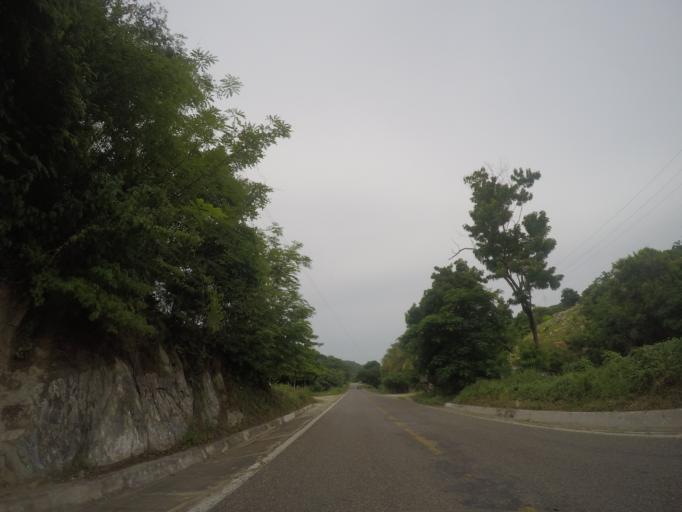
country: MX
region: Oaxaca
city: San Pedro Mixtepec
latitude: 15.9569
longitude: -97.2147
